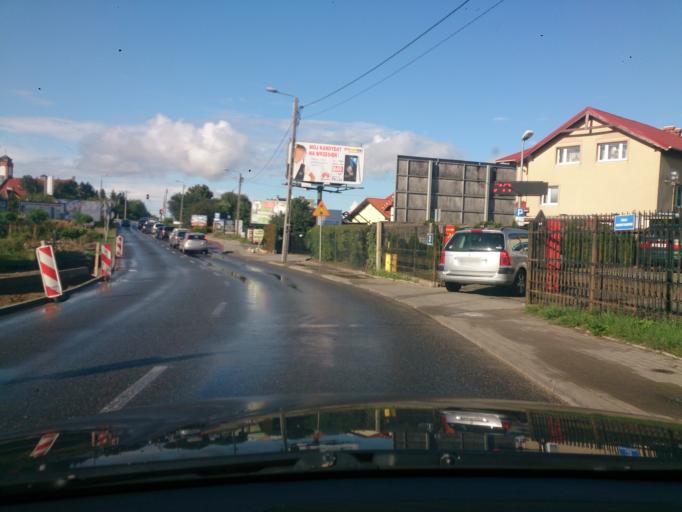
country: PL
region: Pomeranian Voivodeship
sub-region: Gdynia
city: Wielki Kack
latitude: 54.4672
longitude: 18.5093
